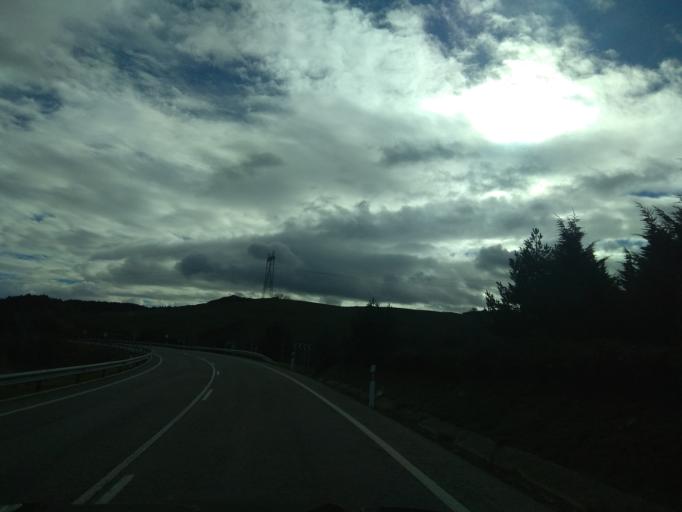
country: ES
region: Castille and Leon
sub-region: Provincia de Burgos
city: Arija
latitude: 43.0004
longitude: -3.8409
